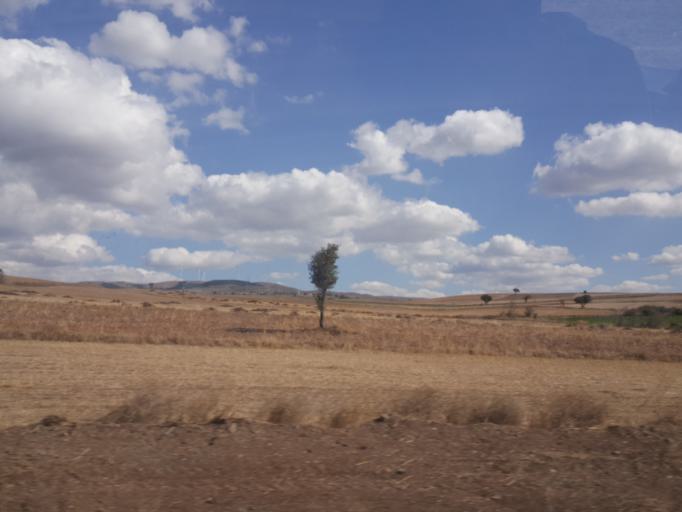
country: TR
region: Tokat
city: Camlibel
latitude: 40.1986
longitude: 36.4666
